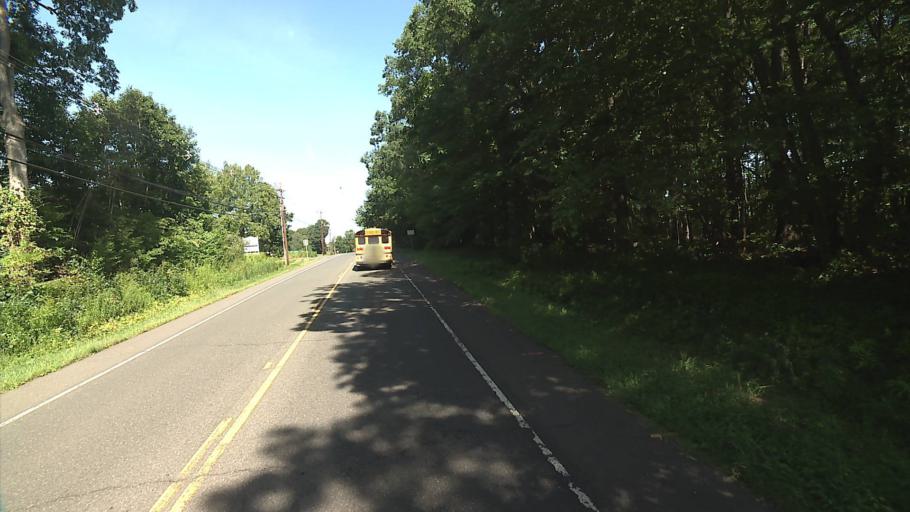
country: US
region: Connecticut
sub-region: New Haven County
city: Middlebury
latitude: 41.5014
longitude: -73.1542
